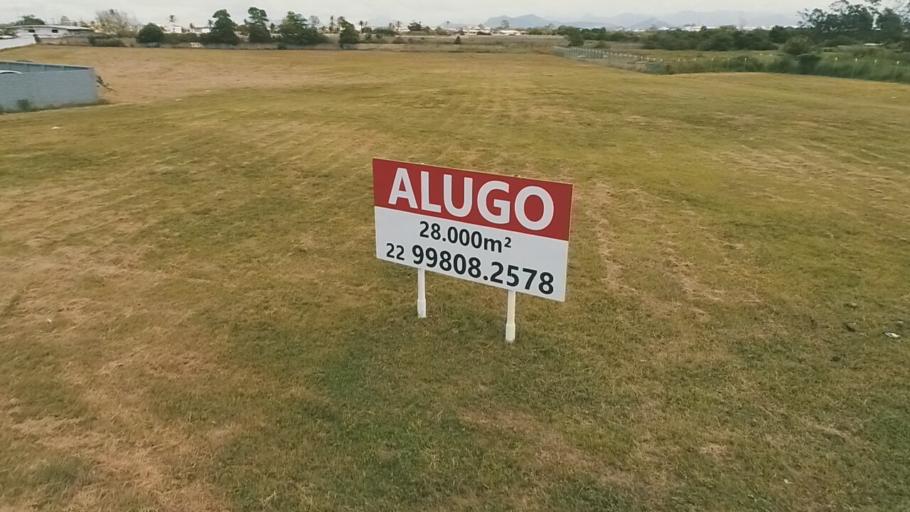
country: BR
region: Rio de Janeiro
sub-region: Macae
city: Macae
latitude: -22.3300
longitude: -41.7526
